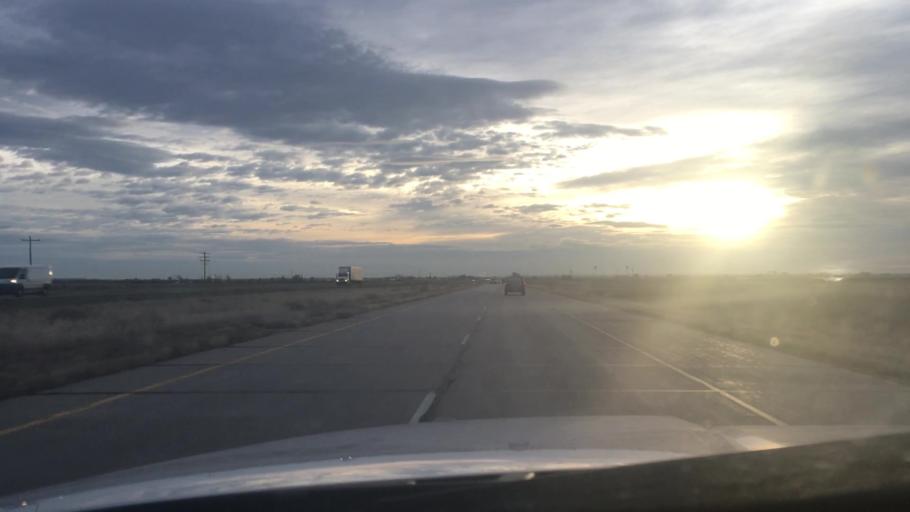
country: US
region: Colorado
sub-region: Morgan County
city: Fort Morgan
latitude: 40.2478
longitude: -103.9925
